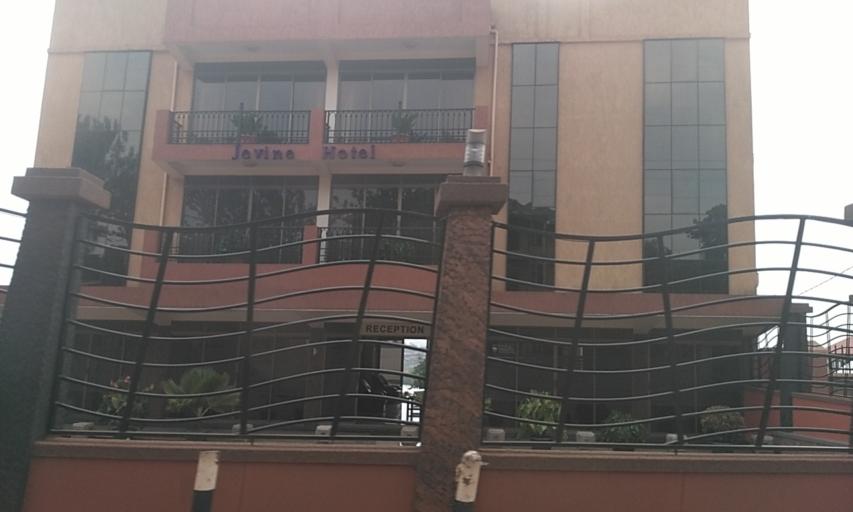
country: UG
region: Central Region
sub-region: Kampala District
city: Kampala
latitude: 0.2976
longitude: 32.5595
